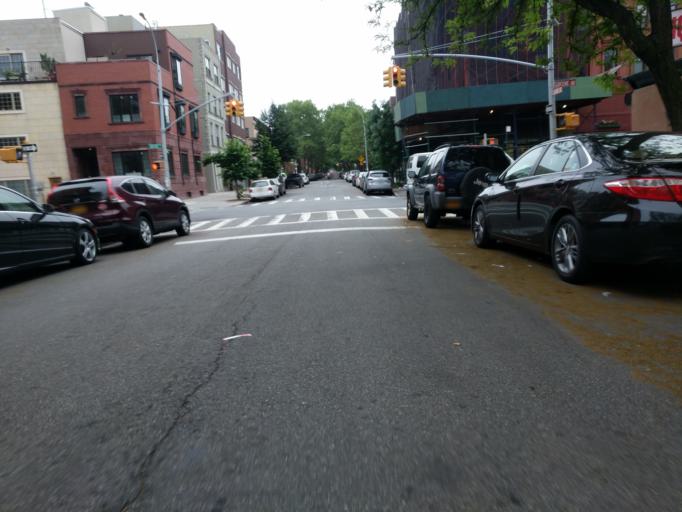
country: US
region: New York
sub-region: Kings County
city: Brooklyn
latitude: 40.6874
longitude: -73.9626
